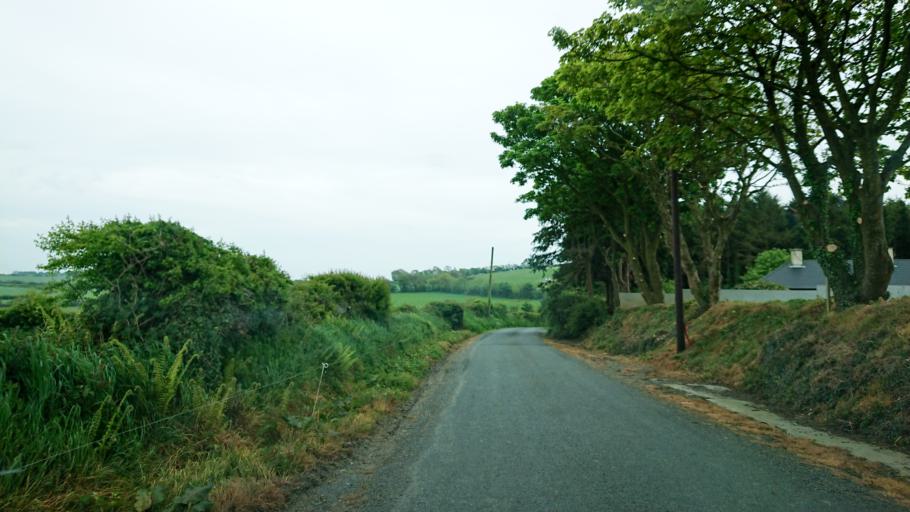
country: IE
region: Munster
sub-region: Waterford
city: Dunmore East
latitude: 52.2226
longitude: -7.0160
